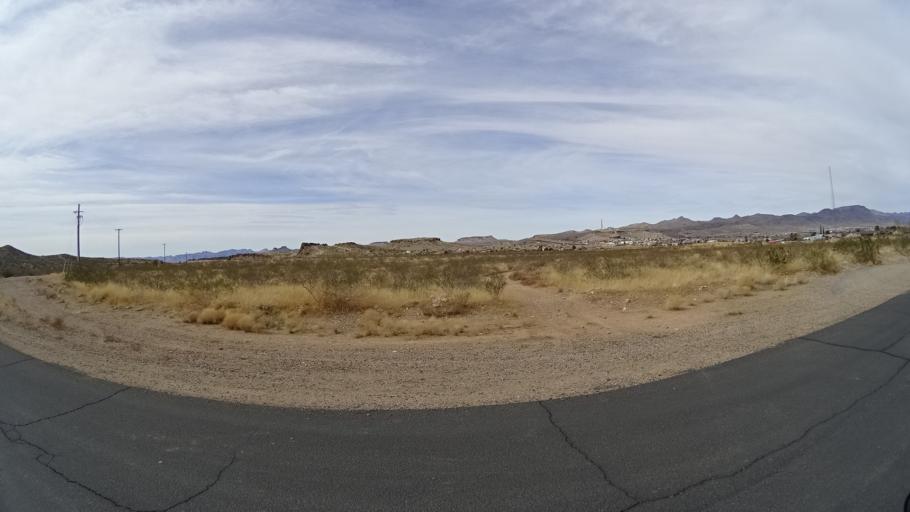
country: US
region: Arizona
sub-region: Mohave County
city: Kingman
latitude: 35.1866
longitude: -114.0180
